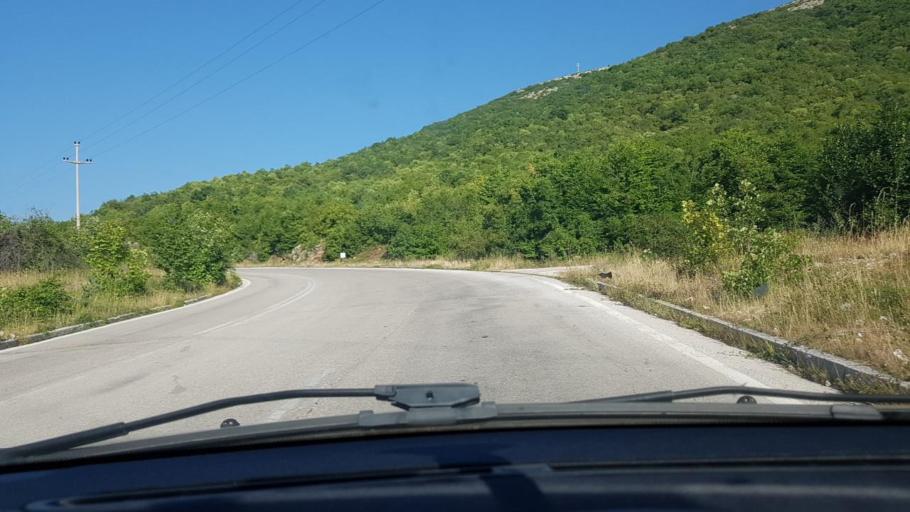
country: BA
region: Federation of Bosnia and Herzegovina
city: Rumboci
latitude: 43.8204
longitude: 17.4724
